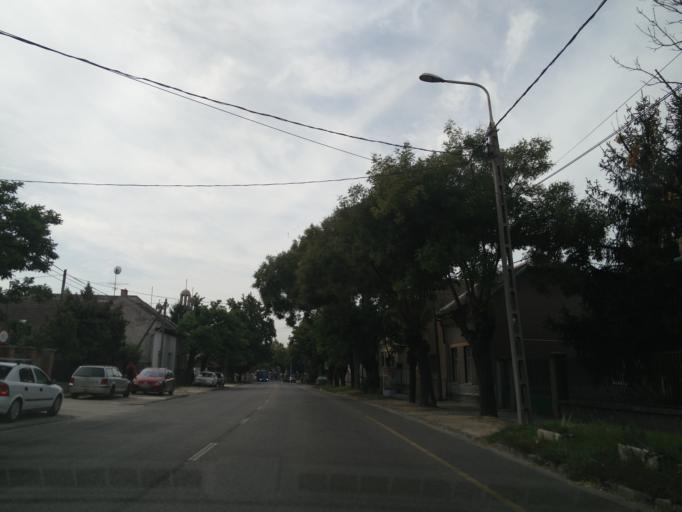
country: HU
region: Budapest
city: Budapest XV. keruelet
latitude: 47.5631
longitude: 19.1247
